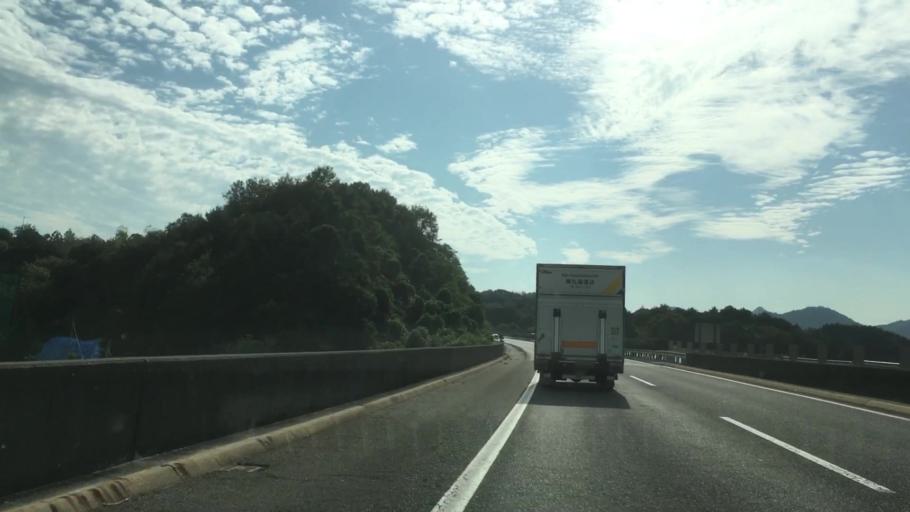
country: JP
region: Yamaguchi
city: Yanai
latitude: 34.0794
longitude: 132.0734
